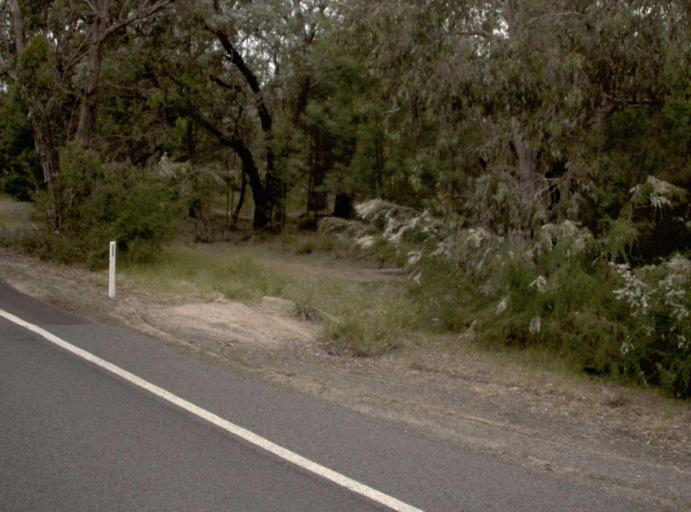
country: AU
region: Victoria
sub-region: Wellington
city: Sale
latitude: -38.3231
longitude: 147.0203
